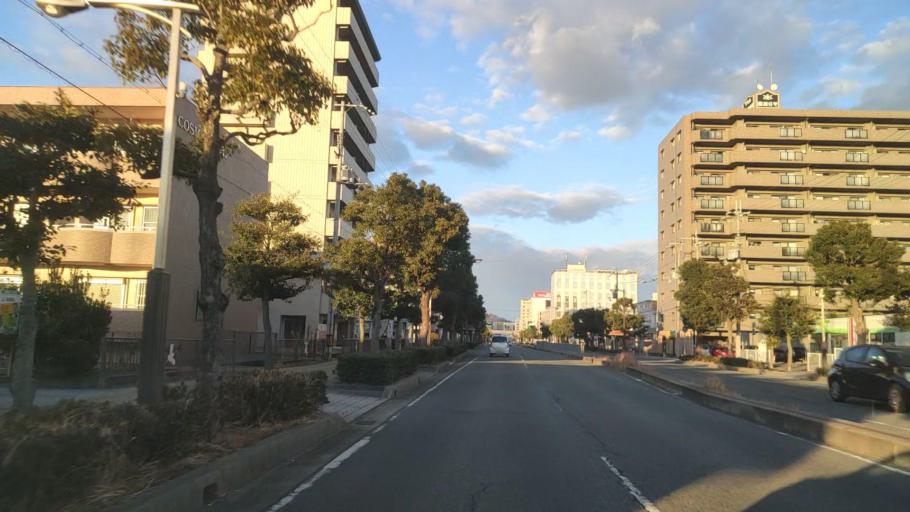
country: JP
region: Hyogo
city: Himeji
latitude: 34.8173
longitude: 134.6906
